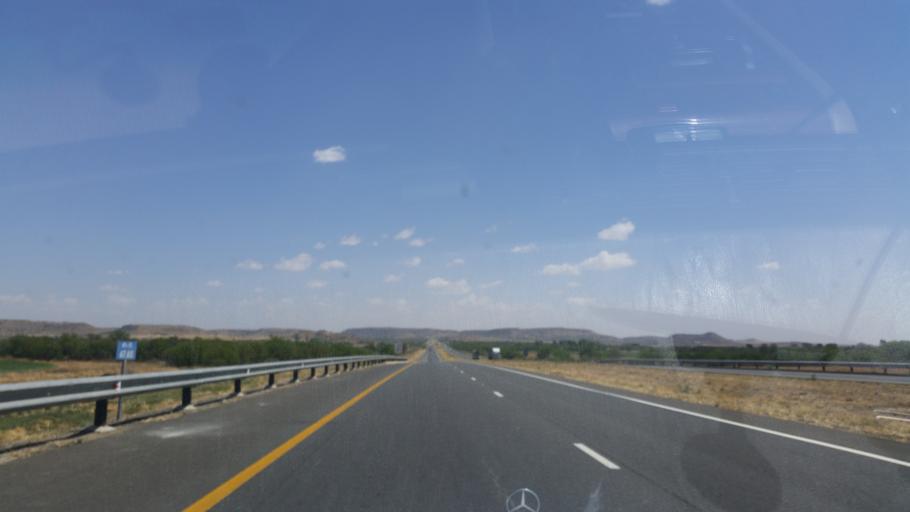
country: ZA
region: Orange Free State
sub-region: Mangaung Metropolitan Municipality
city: Bloemfontein
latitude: -28.9657
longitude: 26.3459
